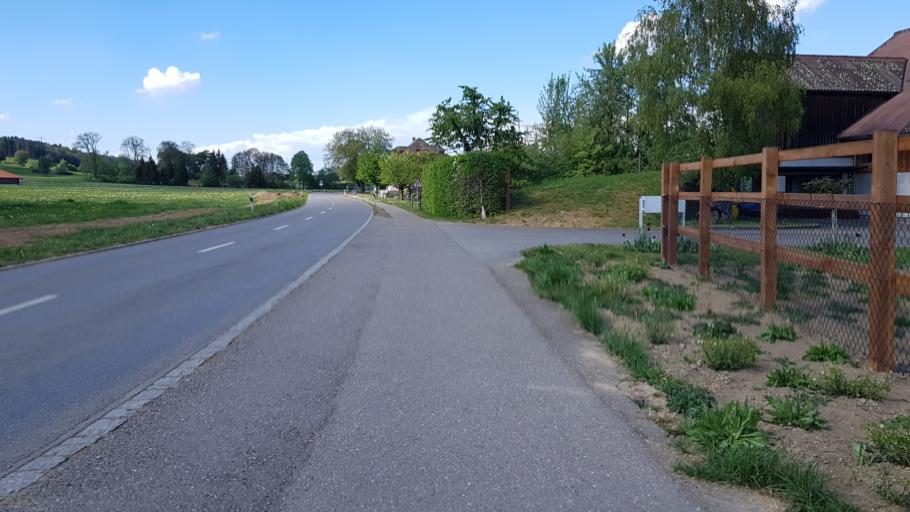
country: CH
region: Lucerne
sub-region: Hochdorf District
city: Hitzkirch
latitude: 47.2109
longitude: 8.2425
